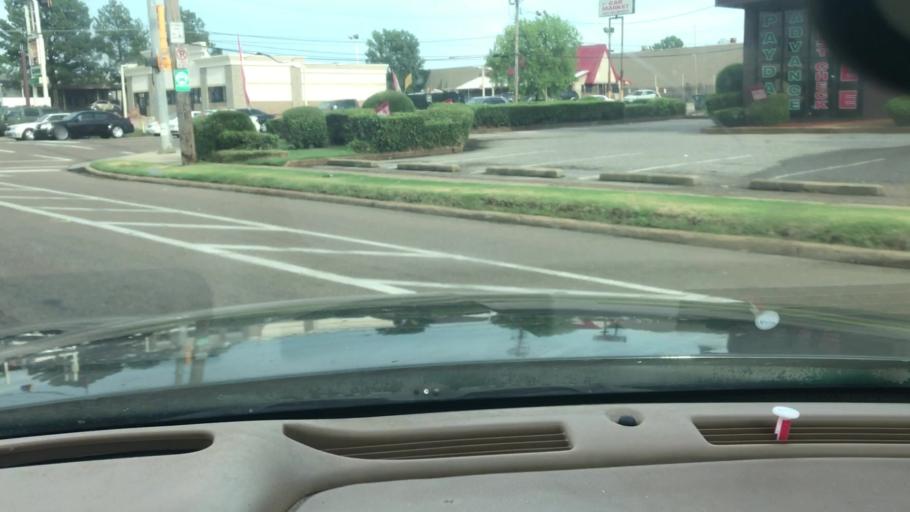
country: US
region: Tennessee
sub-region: Shelby County
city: New South Memphis
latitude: 35.0610
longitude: -90.0077
